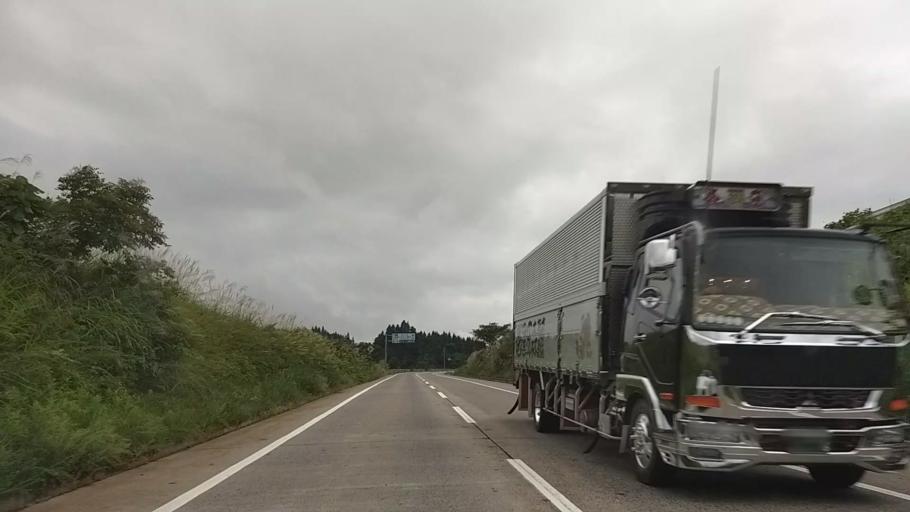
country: JP
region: Nagano
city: Iiyama
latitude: 36.8128
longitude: 138.3409
